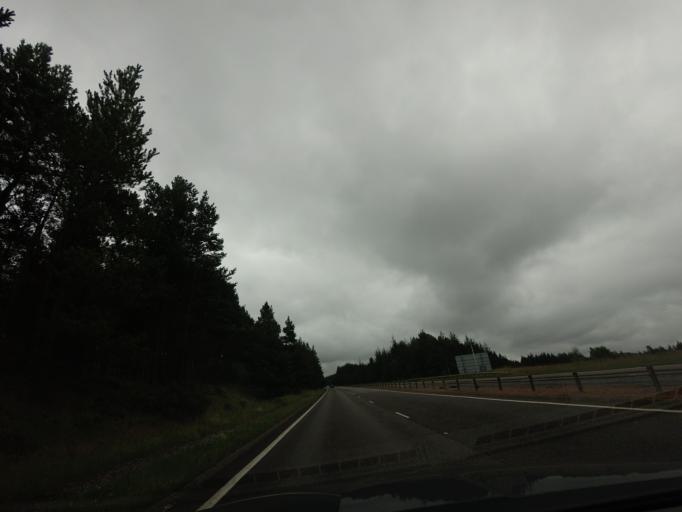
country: GB
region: Scotland
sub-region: Highland
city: Inverness
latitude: 57.4055
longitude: -4.1335
